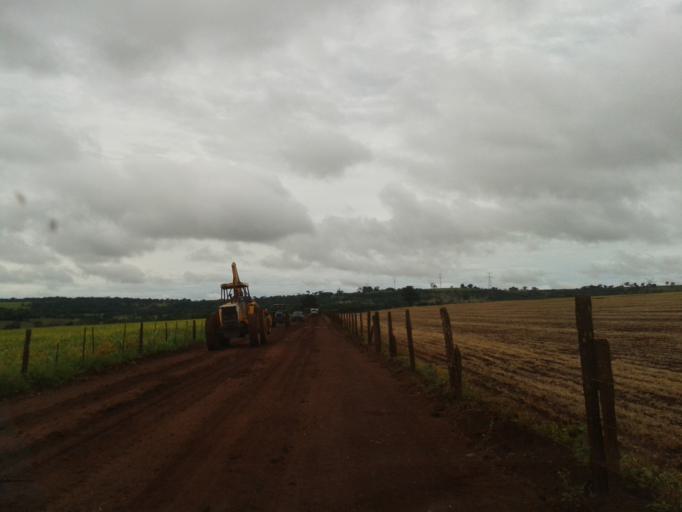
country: BR
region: Minas Gerais
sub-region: Capinopolis
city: Capinopolis
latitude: -18.7154
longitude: -49.7711
